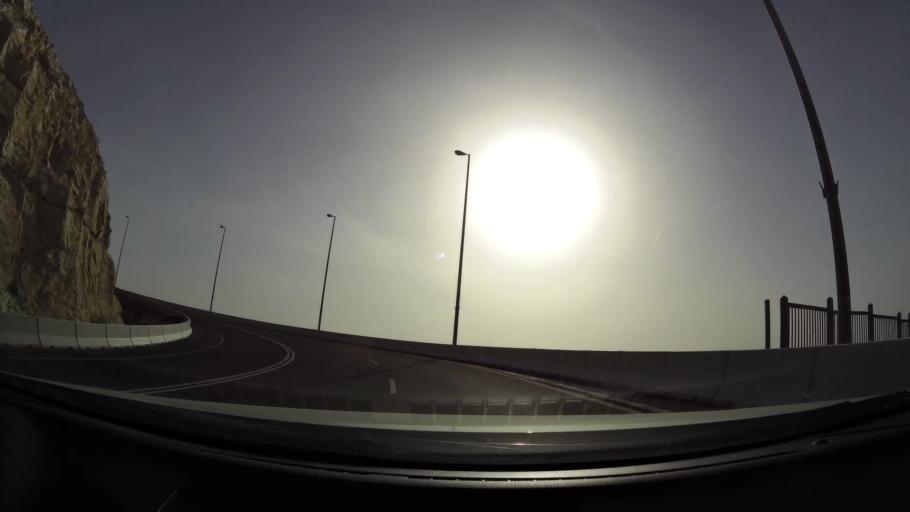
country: AE
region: Abu Dhabi
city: Al Ain
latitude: 24.0851
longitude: 55.7634
